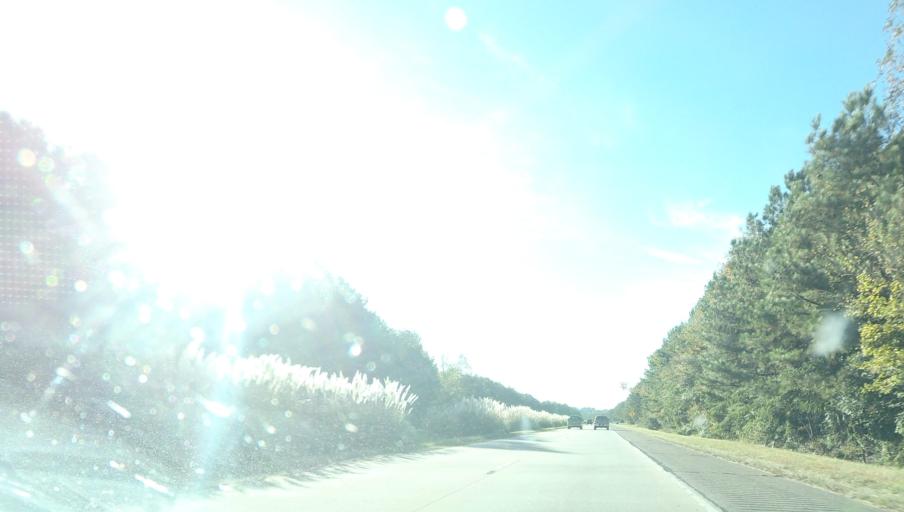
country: US
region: Georgia
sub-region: Muscogee County
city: Columbus
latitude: 32.5545
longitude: -84.9066
